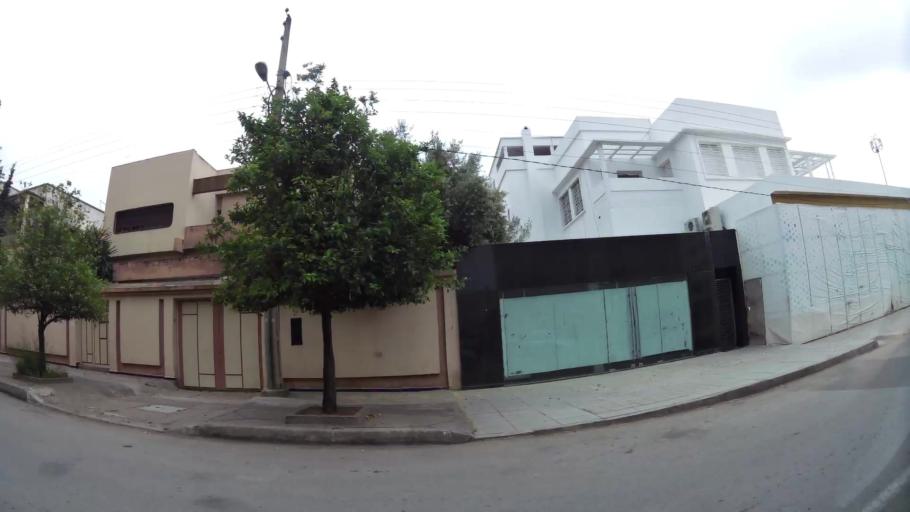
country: MA
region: Fes-Boulemane
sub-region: Fes
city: Fes
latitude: 34.0323
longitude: -5.0089
